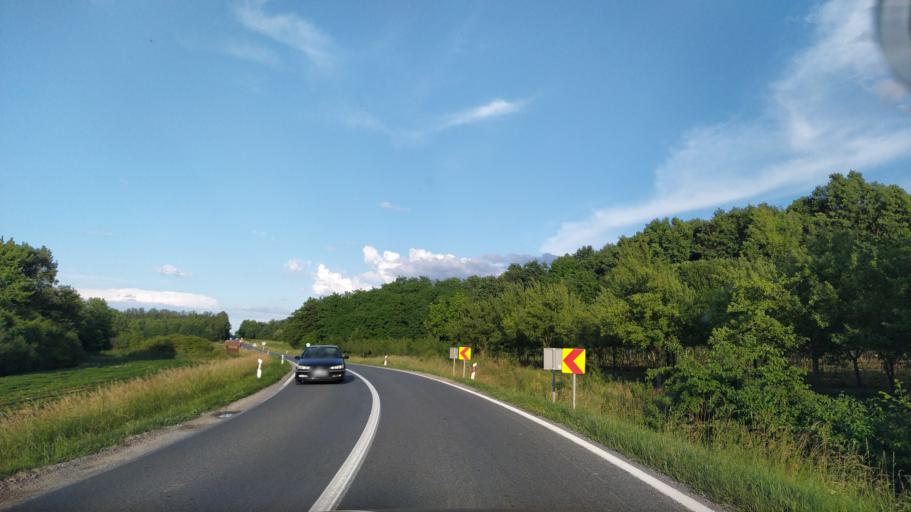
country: HR
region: Virovitick-Podravska
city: Cacinci
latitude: 45.5998
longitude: 17.8386
